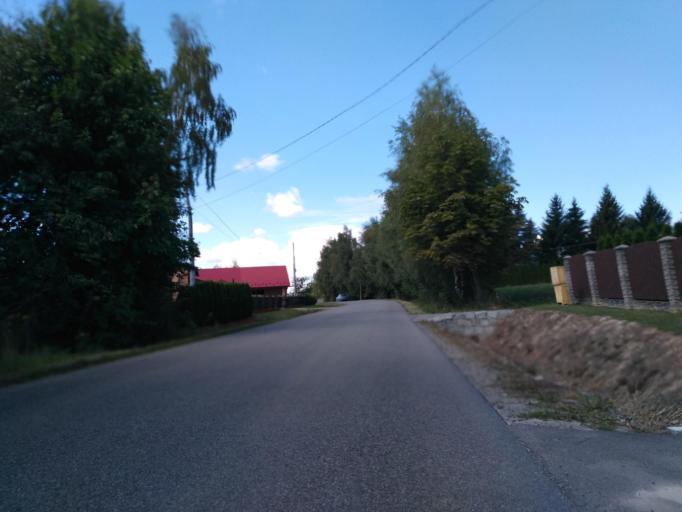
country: PL
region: Subcarpathian Voivodeship
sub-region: Powiat jasielski
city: Skolyszyn
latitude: 49.7802
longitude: 21.3665
